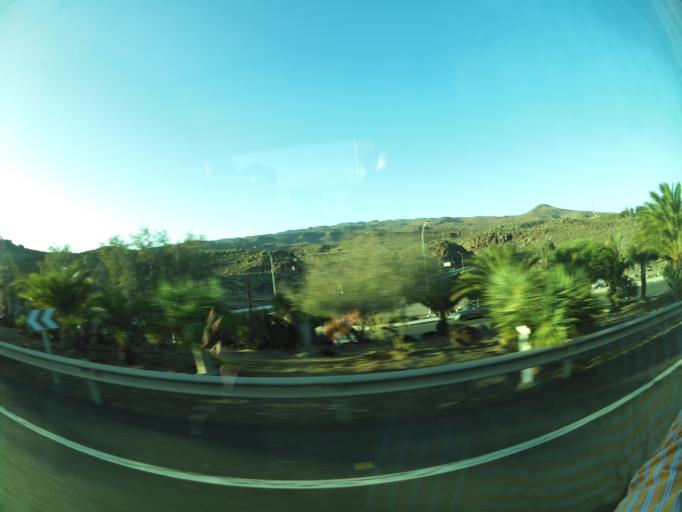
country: ES
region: Canary Islands
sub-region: Provincia de Las Palmas
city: Playa del Ingles
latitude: 27.7777
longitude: -15.5284
